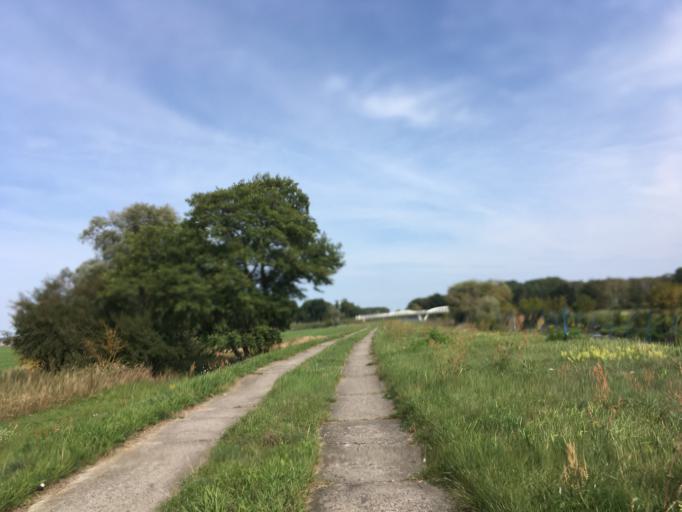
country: PL
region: Lubusz
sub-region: Powiat krosnienski
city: Gubin
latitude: 52.0141
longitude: 14.7264
